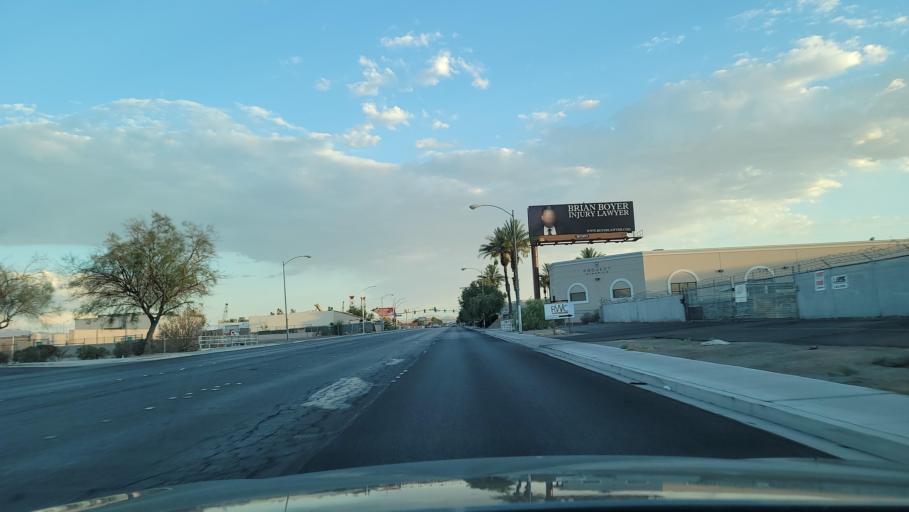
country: US
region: Nevada
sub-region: Clark County
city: Spring Valley
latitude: 36.0961
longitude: -115.1993
